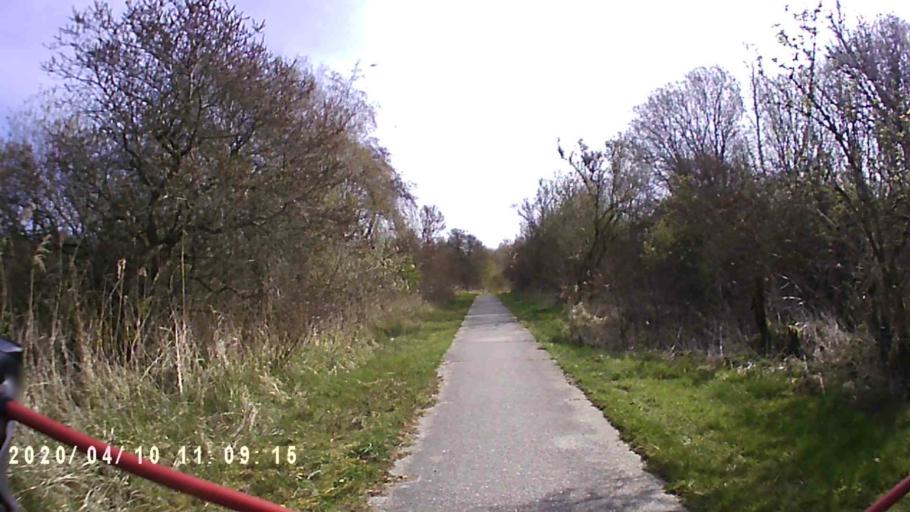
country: NL
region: Groningen
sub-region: Gemeente De Marne
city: Ulrum
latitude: 53.3919
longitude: 6.2432
